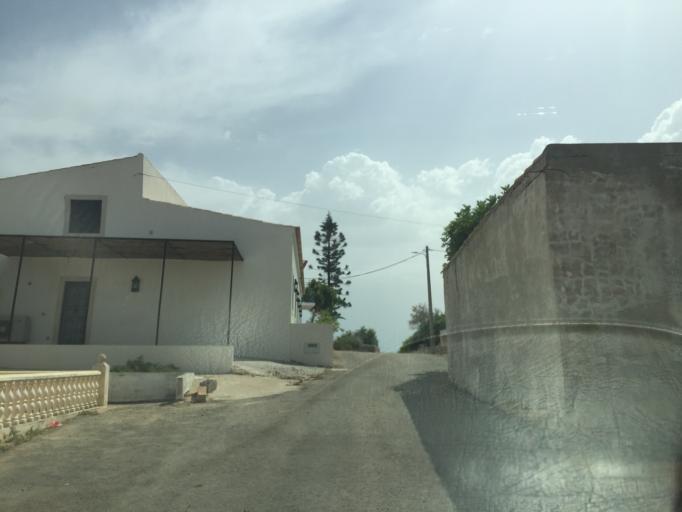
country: PT
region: Faro
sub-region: Loule
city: Boliqueime
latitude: 37.1290
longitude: -8.1406
